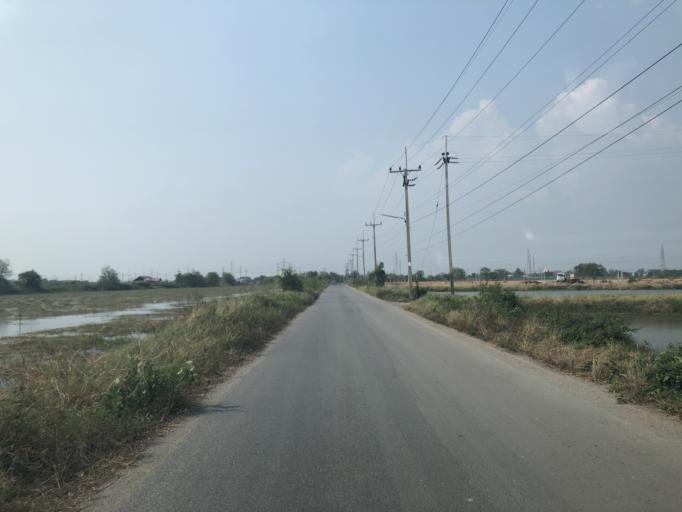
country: TH
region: Chachoengsao
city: Bang Pakong
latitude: 13.5133
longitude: 100.9409
